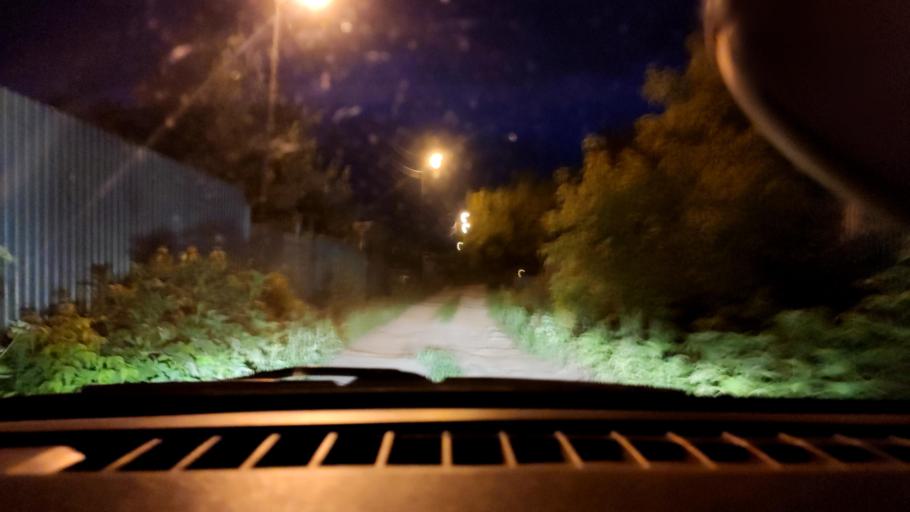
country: RU
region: Samara
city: Smyshlyayevka
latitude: 53.2352
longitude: 50.3161
